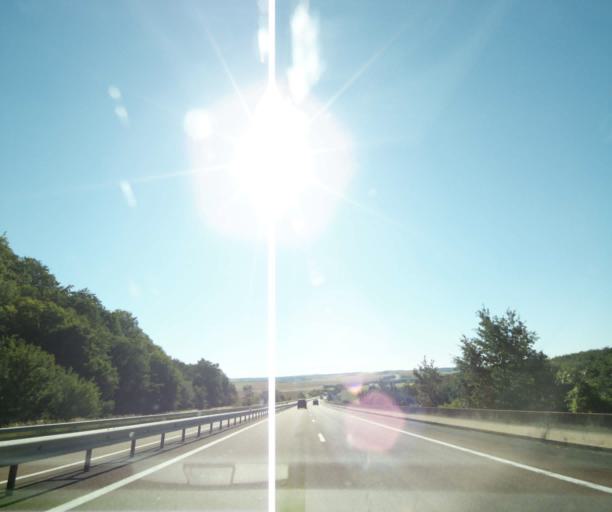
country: FR
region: Champagne-Ardenne
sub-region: Departement de l'Aube
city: Bar-sur-Aube
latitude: 48.1383
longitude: 4.6329
